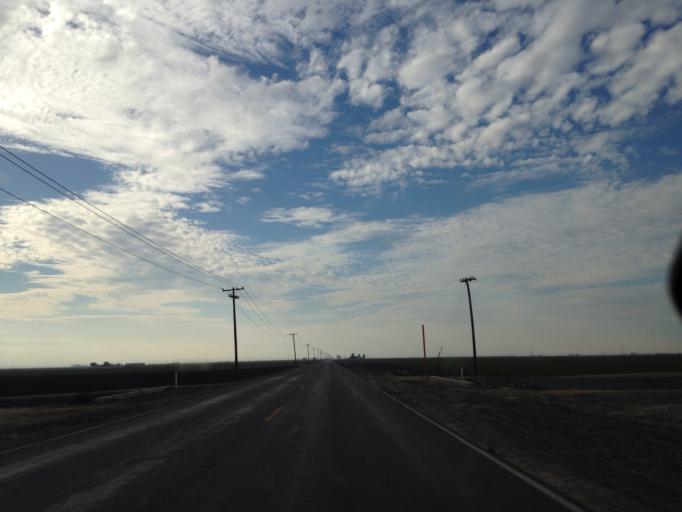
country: US
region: California
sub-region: Kern County
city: Buttonwillow
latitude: 35.4423
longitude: -119.5026
